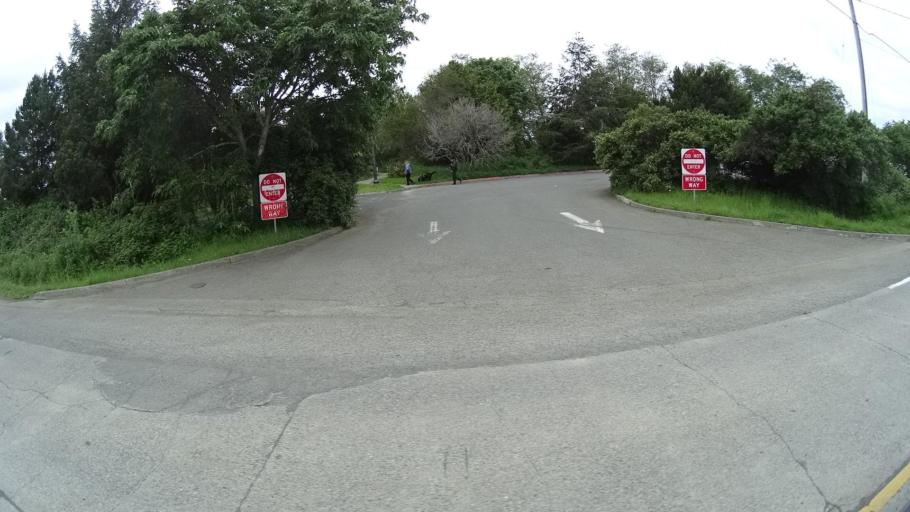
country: US
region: California
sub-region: Humboldt County
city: Arcata
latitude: 40.8585
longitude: -124.0896
